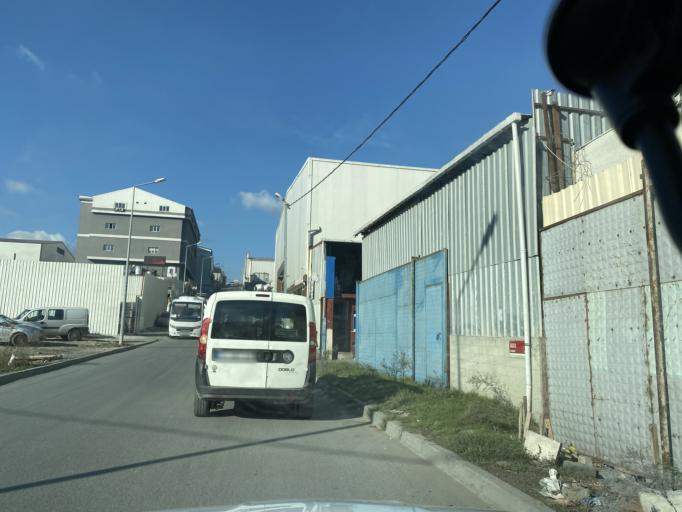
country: TR
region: Istanbul
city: Esenyurt
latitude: 41.0521
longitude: 28.6481
